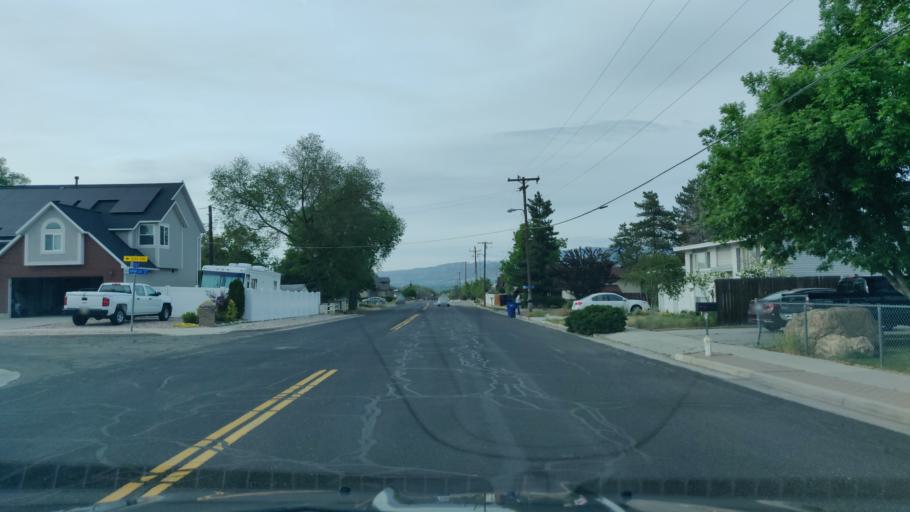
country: US
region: Utah
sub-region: Salt Lake County
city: Little Cottonwood Creek Valley
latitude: 40.6216
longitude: -111.8439
